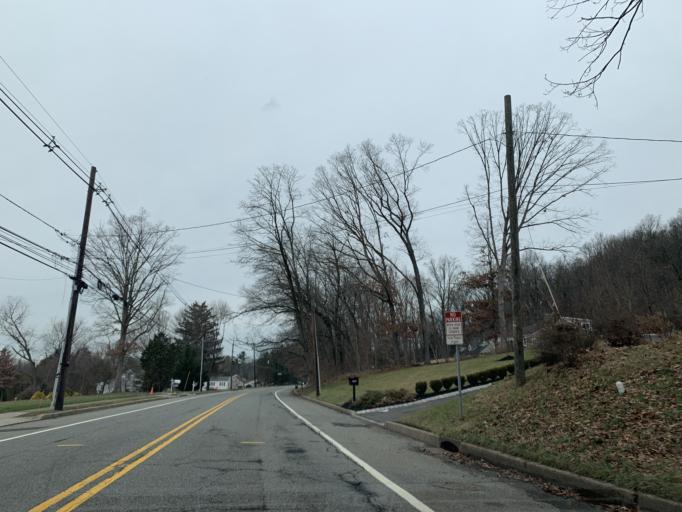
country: US
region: New Jersey
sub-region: Somerset County
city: Martinsville
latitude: 40.6129
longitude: -74.5788
